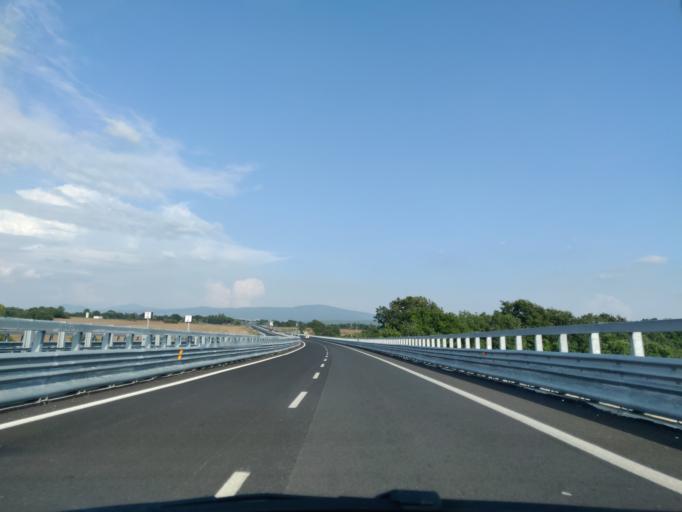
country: IT
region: Latium
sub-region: Provincia di Viterbo
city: Monte Romano
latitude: 42.2974
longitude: 11.9621
